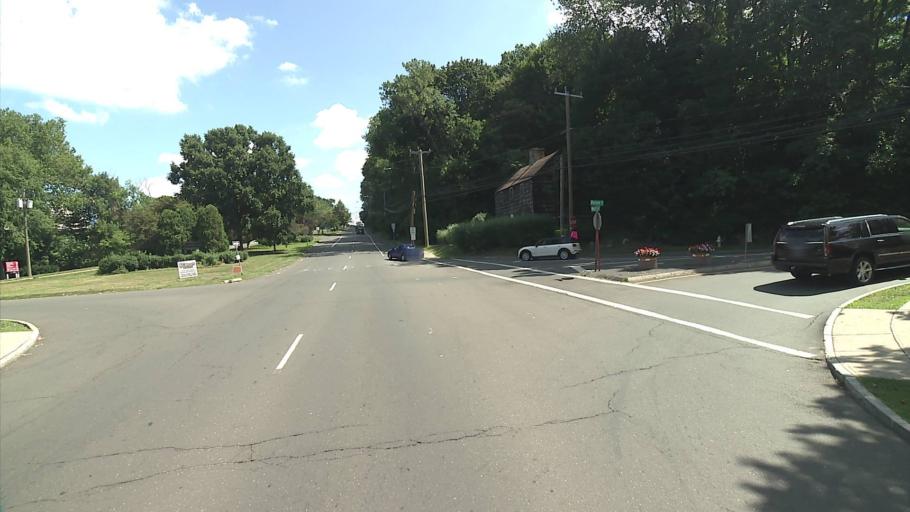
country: US
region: Connecticut
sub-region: Fairfield County
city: Byram
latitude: 41.0124
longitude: -73.6550
